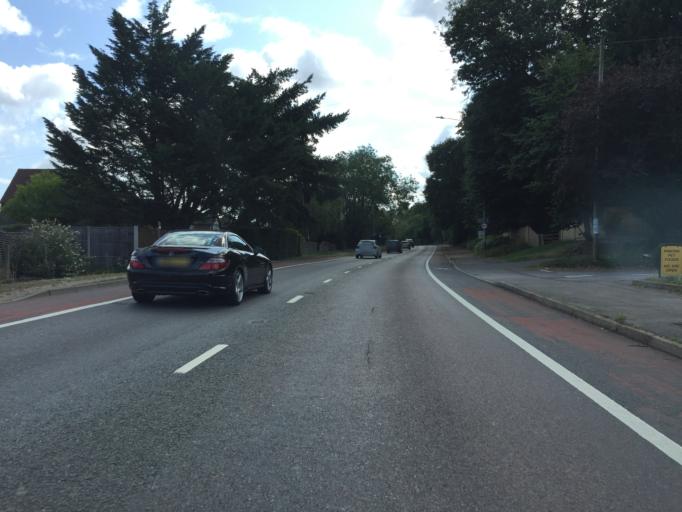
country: GB
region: England
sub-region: Kent
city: Aylesford
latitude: 51.2975
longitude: 0.4618
